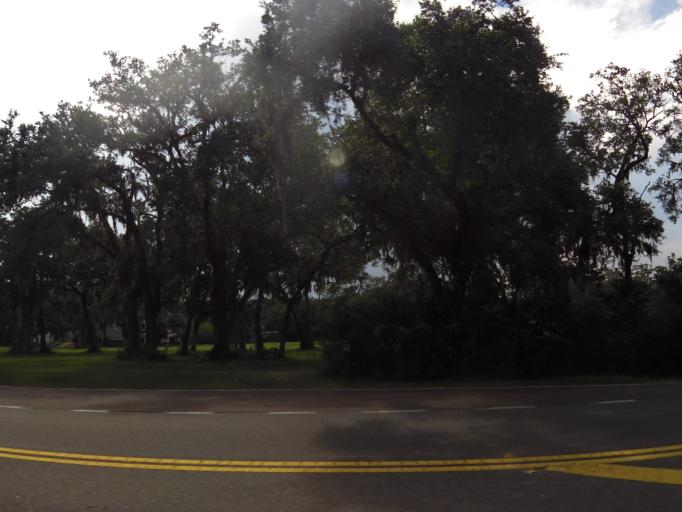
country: US
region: Florida
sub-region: Nassau County
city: Fernandina Beach
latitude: 30.6106
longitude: -81.4521
